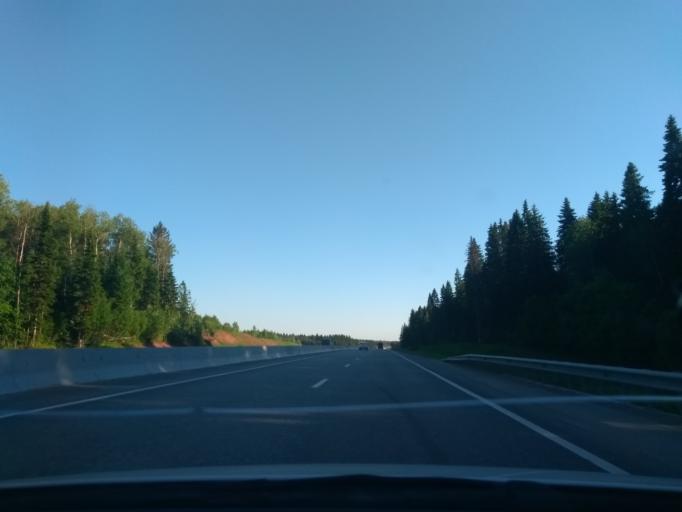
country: RU
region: Perm
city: Ferma
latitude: 57.9666
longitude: 56.4004
